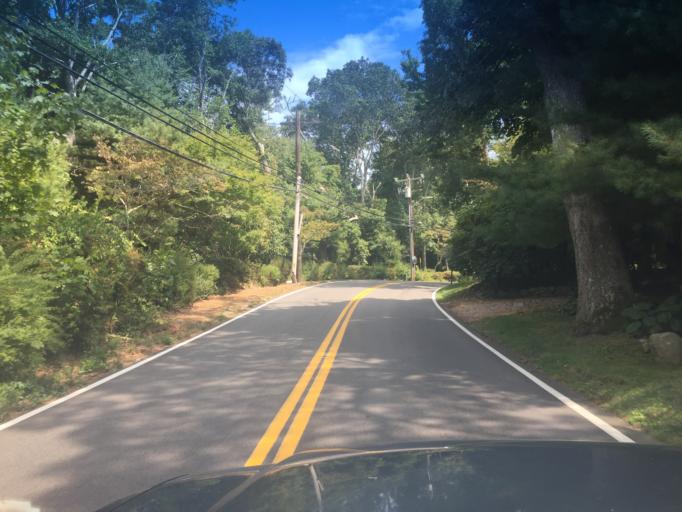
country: US
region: Massachusetts
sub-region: Barnstable County
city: Falmouth
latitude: 41.5710
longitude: -70.6224
